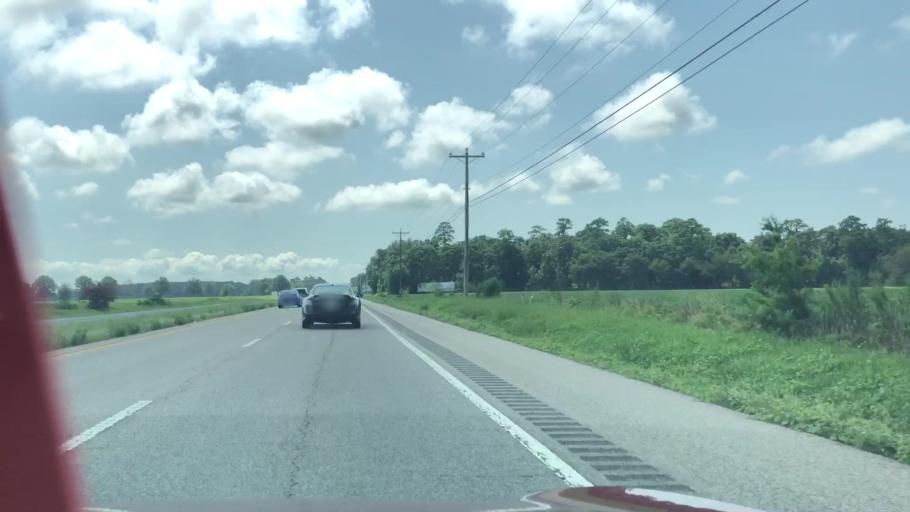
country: US
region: Virginia
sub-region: Northampton County
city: Cape Charles
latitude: 37.2456
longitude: -75.9720
